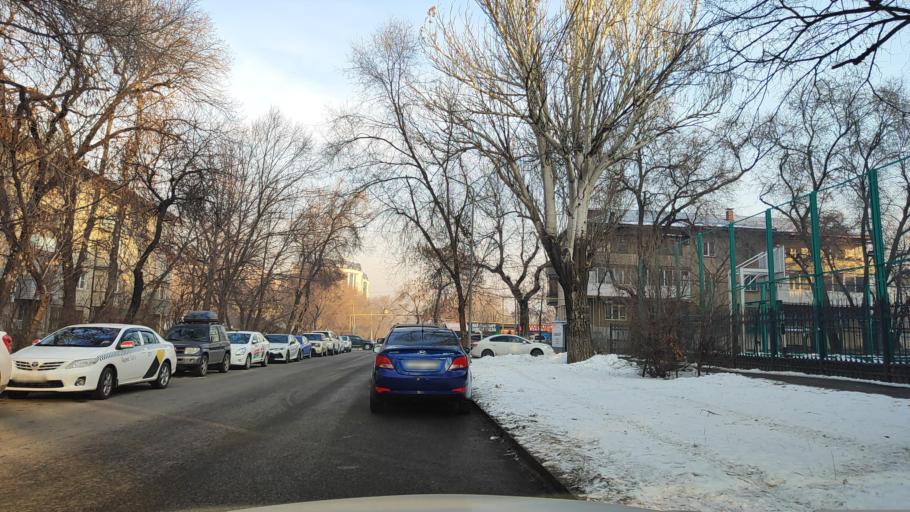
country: KZ
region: Almaty Qalasy
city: Almaty
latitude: 43.2575
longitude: 76.9592
